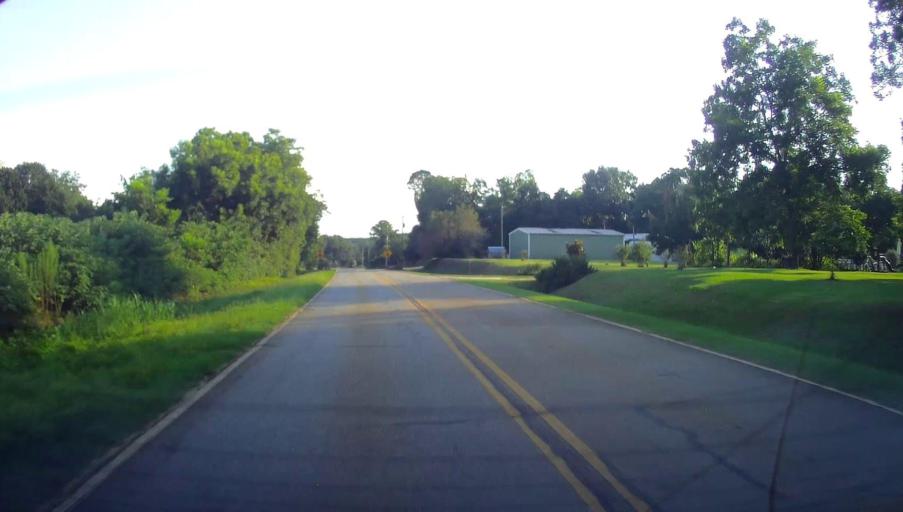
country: US
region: Georgia
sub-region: Peach County
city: Fort Valley
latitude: 32.5894
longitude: -83.8453
